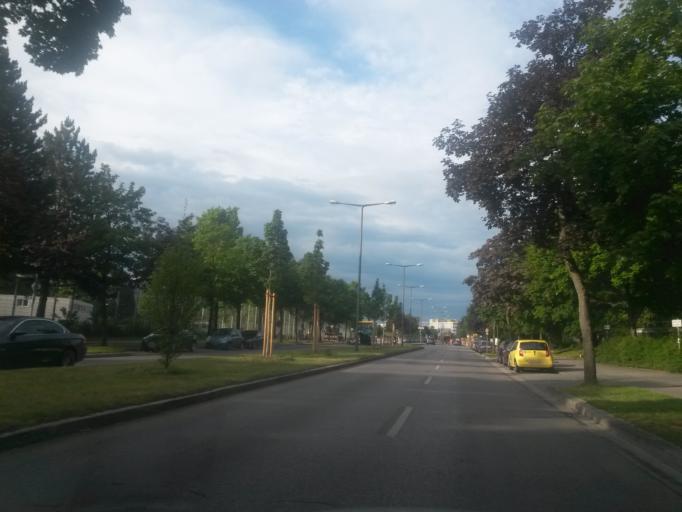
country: DE
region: Bavaria
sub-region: Upper Bavaria
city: Neubiberg
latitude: 48.0975
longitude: 11.6563
